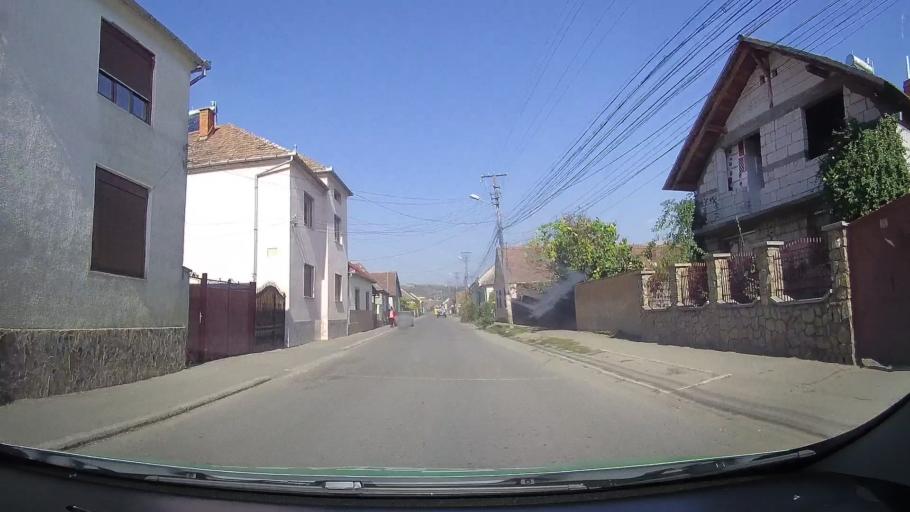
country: RO
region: Arad
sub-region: Oras Lipova
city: Lipova
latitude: 46.0853
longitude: 21.6901
